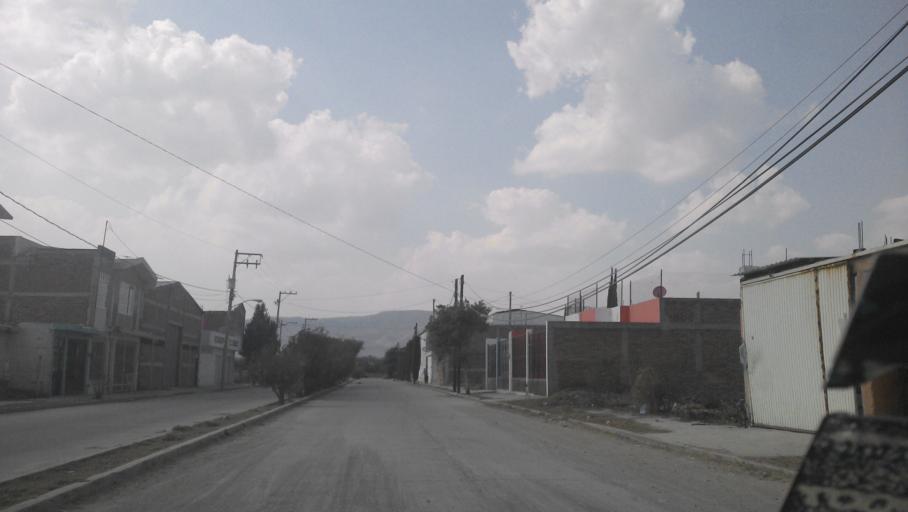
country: MX
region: Guanajuato
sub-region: San Francisco del Rincon
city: Fraccionamiento Villa Jardin
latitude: 20.9996
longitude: -101.8529
